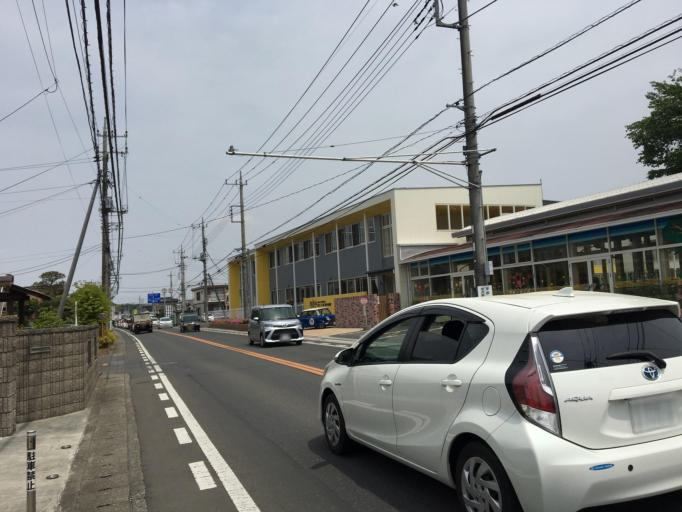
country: JP
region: Tochigi
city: Oyama
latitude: 36.3357
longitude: 139.8170
